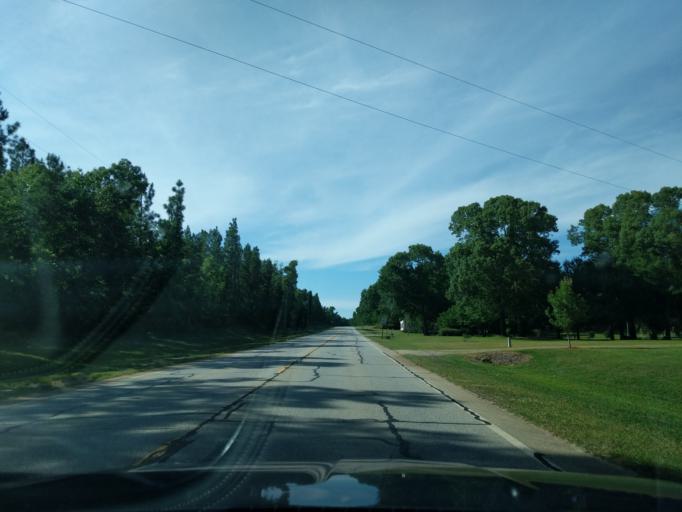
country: US
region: Georgia
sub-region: Jefferson County
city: Wrens
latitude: 33.2401
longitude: -82.3850
